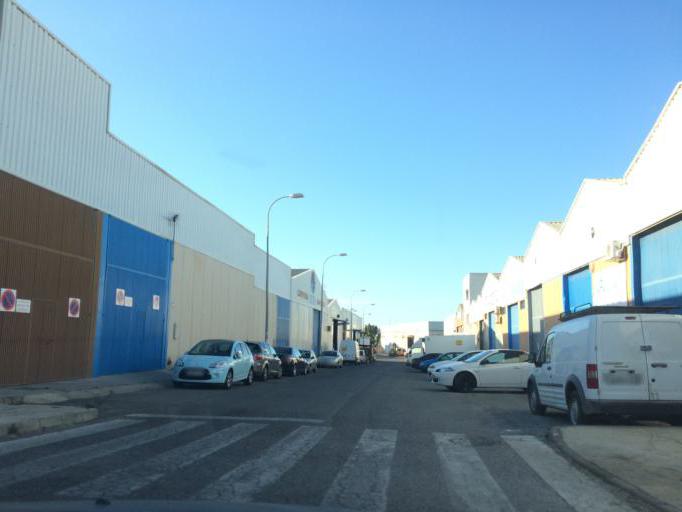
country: ES
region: Andalusia
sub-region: Provincia de Almeria
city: Viator
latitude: 36.8824
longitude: -2.4196
